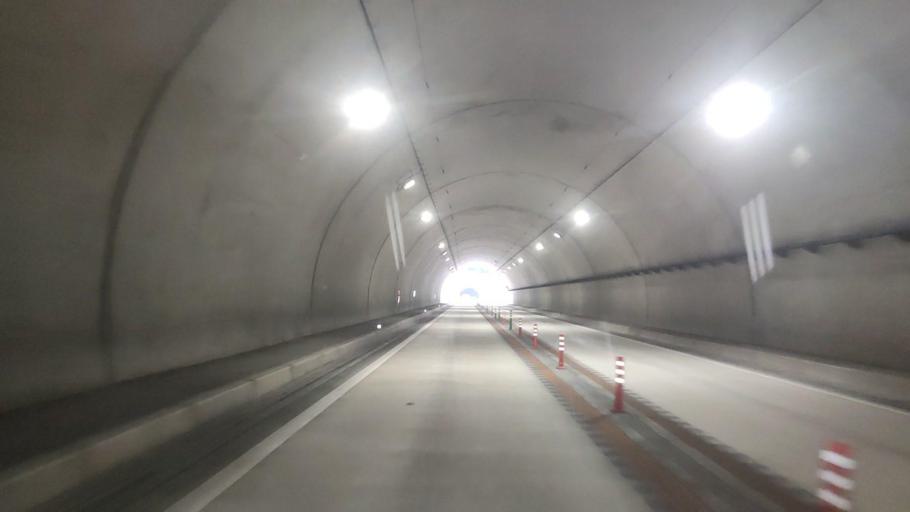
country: JP
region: Wakayama
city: Tanabe
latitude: 33.5653
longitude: 135.4960
